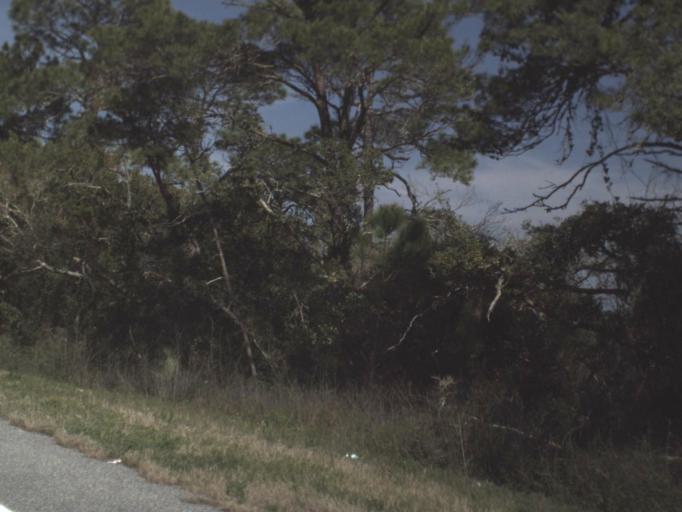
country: US
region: Florida
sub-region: Franklin County
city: Eastpoint
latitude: 29.7863
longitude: -84.7677
